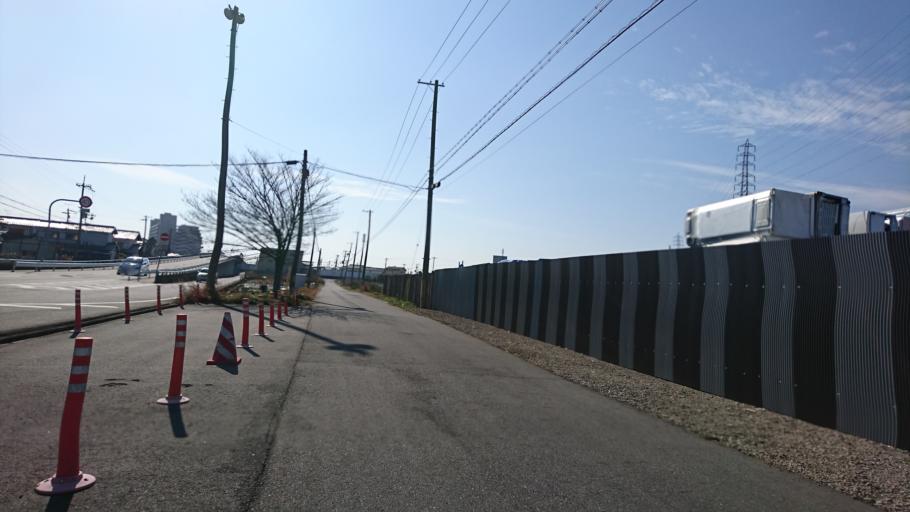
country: JP
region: Hyogo
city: Kakogawacho-honmachi
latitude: 34.7861
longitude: 134.8297
